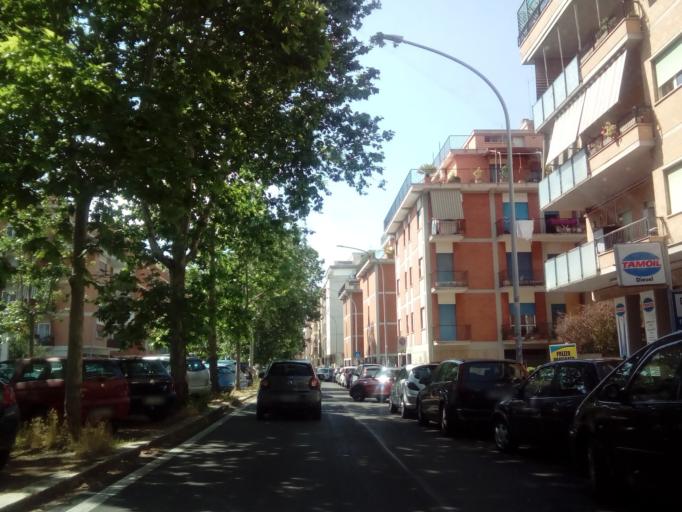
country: IT
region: Latium
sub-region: Citta metropolitana di Roma Capitale
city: Rome
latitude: 41.8556
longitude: 12.5593
